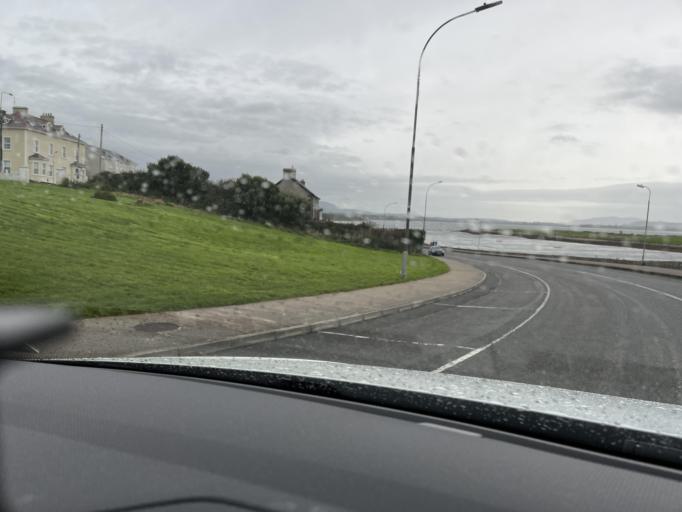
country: IE
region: Connaught
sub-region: Sligo
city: Strandhill
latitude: 54.3050
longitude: -8.5669
